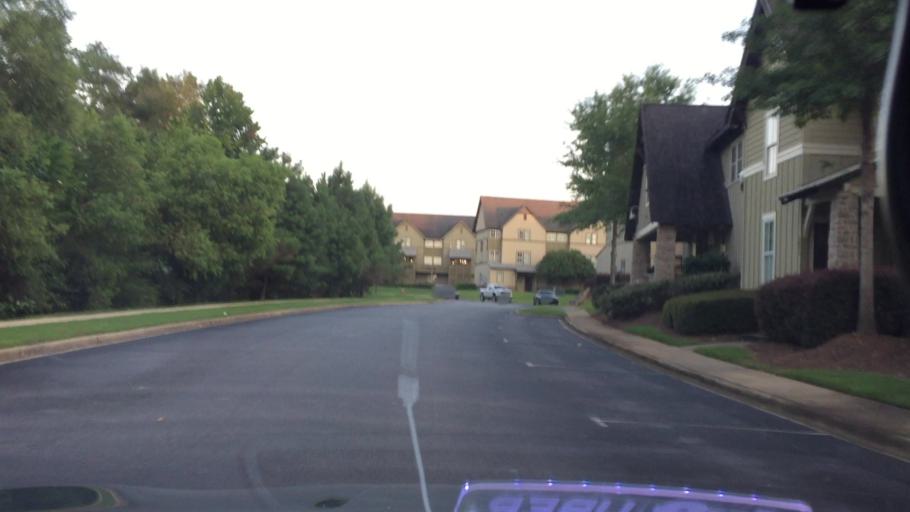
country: US
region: Alabama
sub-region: Lee County
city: Auburn
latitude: 32.6187
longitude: -85.4696
